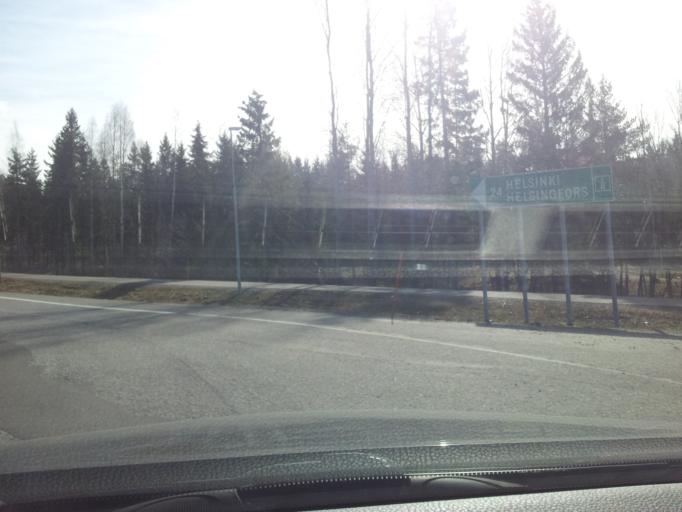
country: FI
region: Uusimaa
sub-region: Helsinki
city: Kirkkonummi
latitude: 60.1365
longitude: 24.5349
